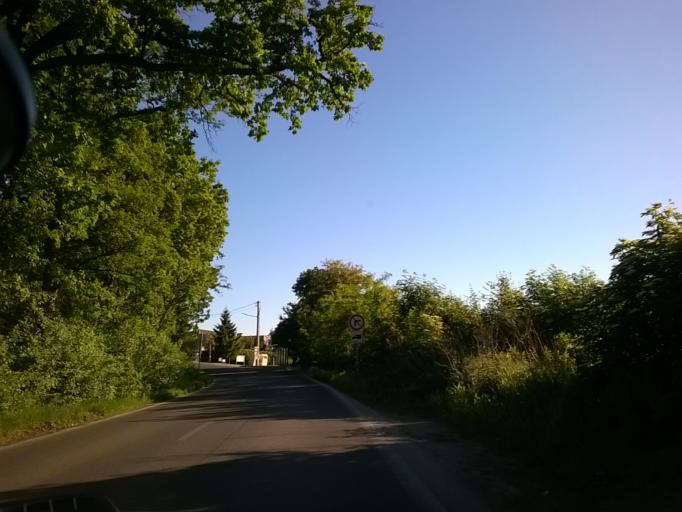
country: SK
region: Nitriansky
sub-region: Okres Nitra
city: Nitra
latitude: 48.3418
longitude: 18.0870
